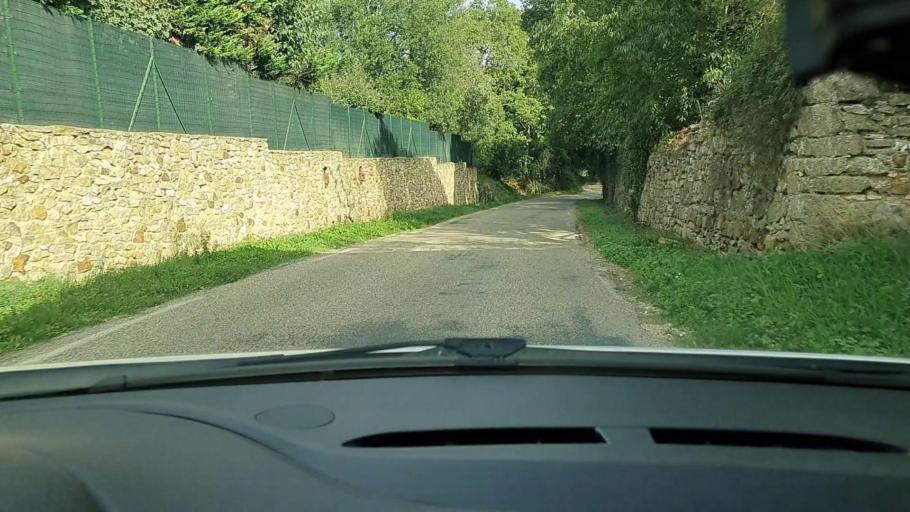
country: FR
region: Languedoc-Roussillon
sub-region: Departement du Gard
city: Saint-Quentin-la-Poterie
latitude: 44.1118
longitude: 4.4143
